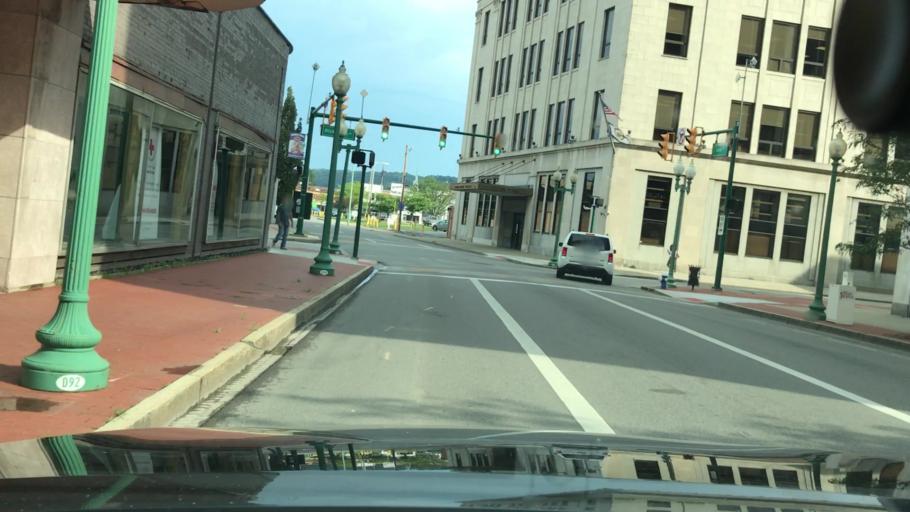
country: US
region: West Virginia
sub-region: Kanawha County
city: Charleston
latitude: 38.3501
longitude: -81.6327
